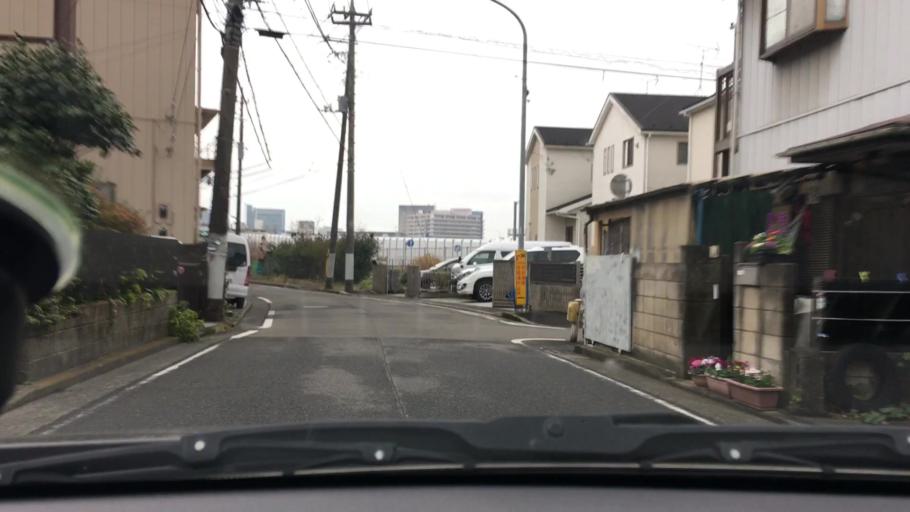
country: JP
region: Kanagawa
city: Yokohama
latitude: 35.5176
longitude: 139.6056
